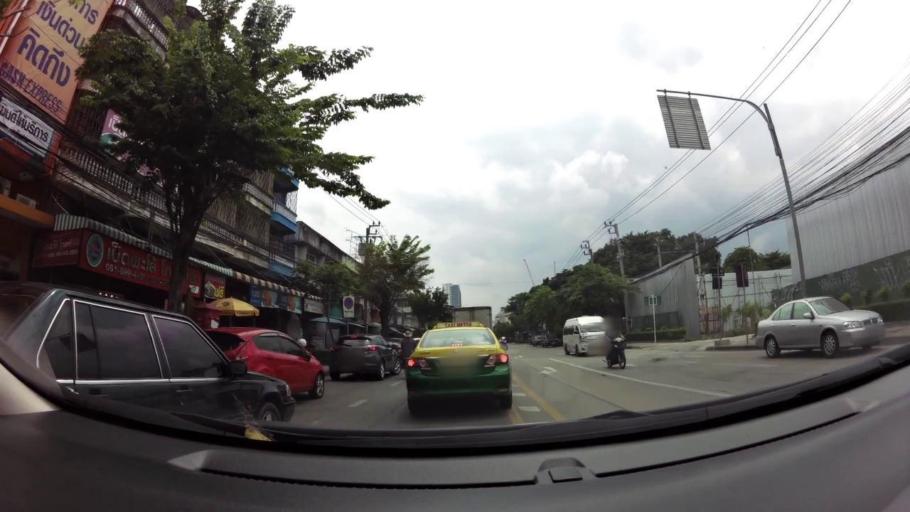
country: TH
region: Bangkok
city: Bang Na
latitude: 13.6786
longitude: 100.6173
